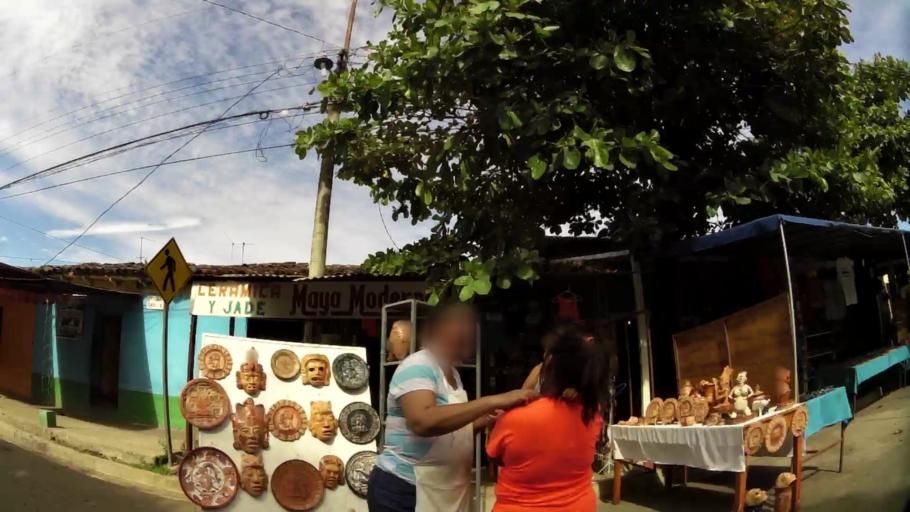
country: SV
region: Santa Ana
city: Chalchuapa
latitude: 13.9806
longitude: -89.6745
